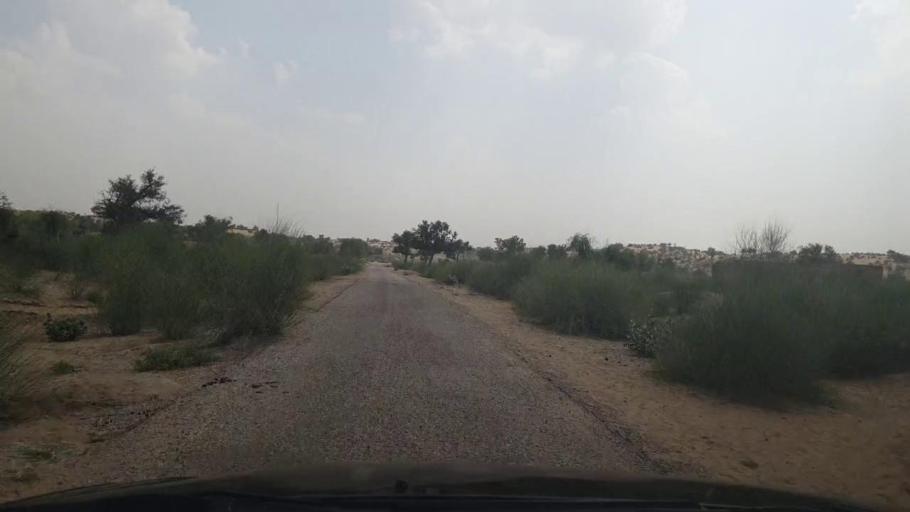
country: PK
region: Sindh
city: Islamkot
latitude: 24.9907
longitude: 70.4972
